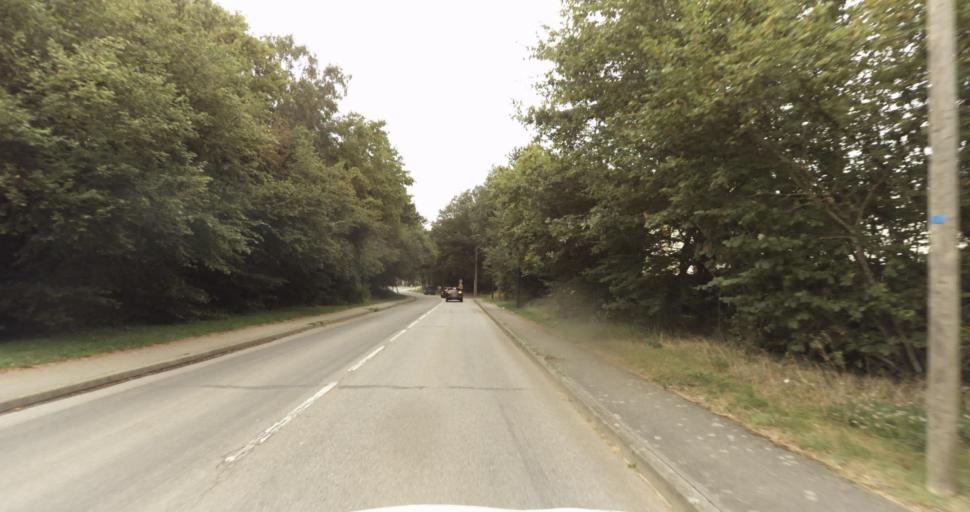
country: FR
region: Haute-Normandie
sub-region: Departement de l'Eure
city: Gravigny
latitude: 49.0331
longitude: 1.1774
